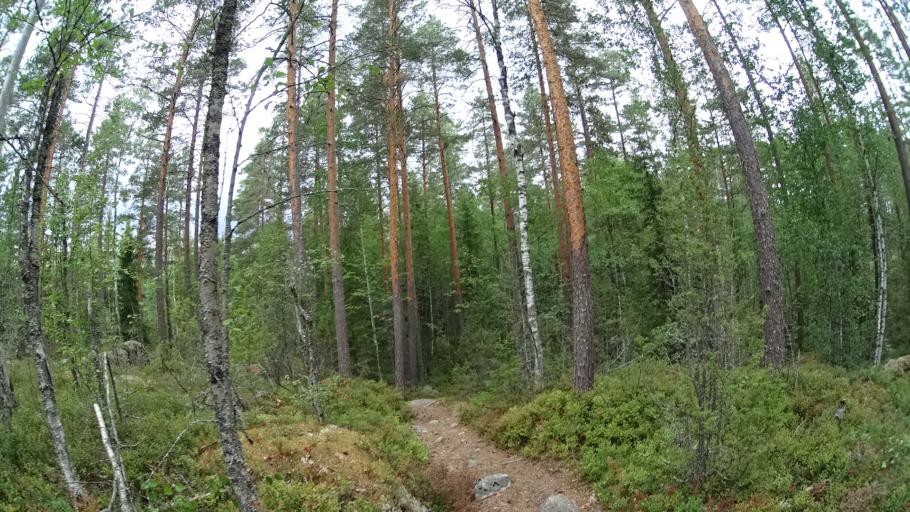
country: FI
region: Uusimaa
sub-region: Helsinki
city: Espoo
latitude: 60.3073
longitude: 24.5790
